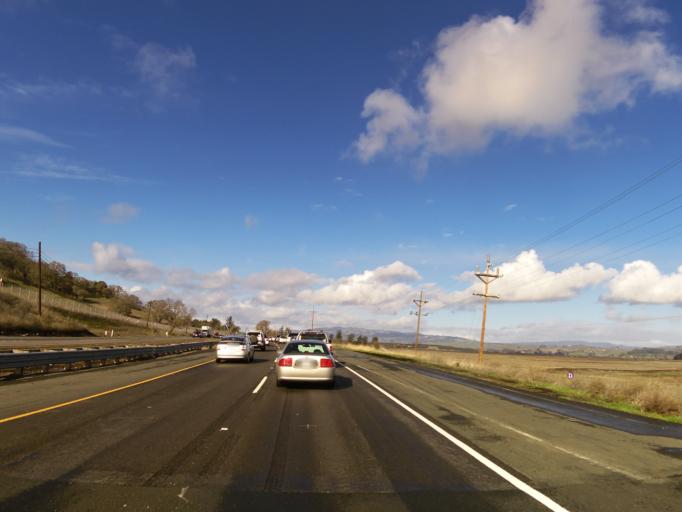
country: US
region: California
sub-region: Marin County
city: Novato
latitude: 38.1444
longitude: -122.5645
